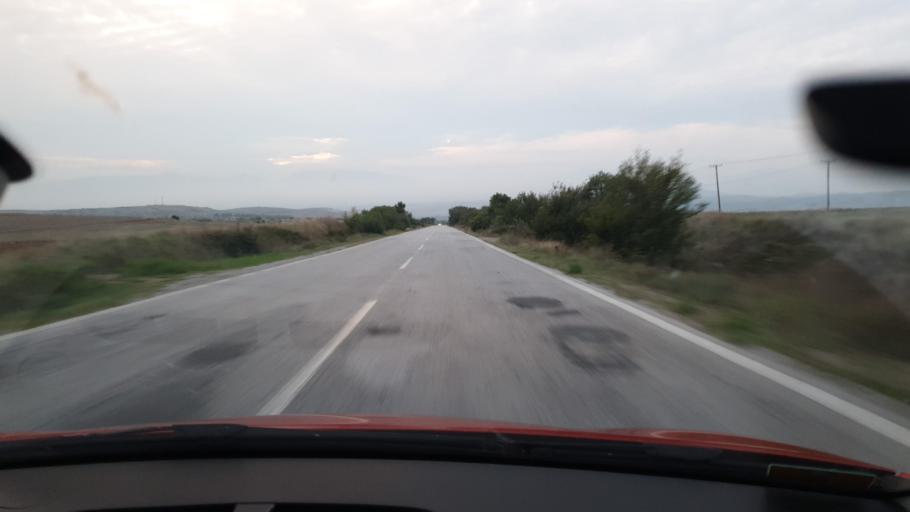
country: GR
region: Central Macedonia
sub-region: Nomos Kilkis
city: Polykastro
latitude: 41.0075
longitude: 22.6940
